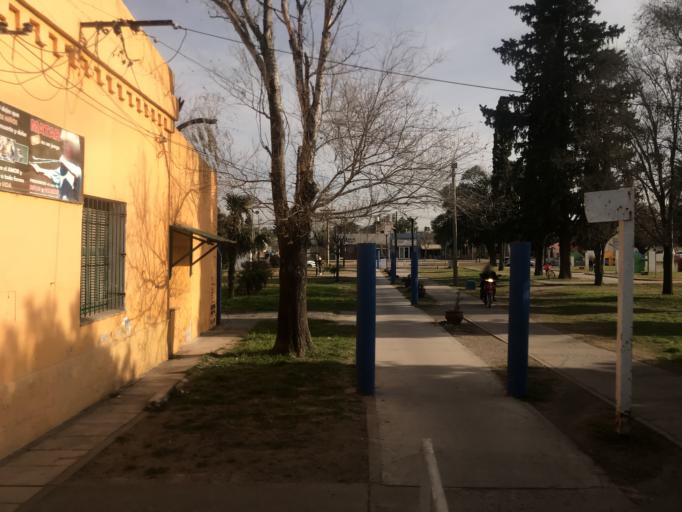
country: AR
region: Cordoba
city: Laguna Larga
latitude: -31.7772
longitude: -63.8029
